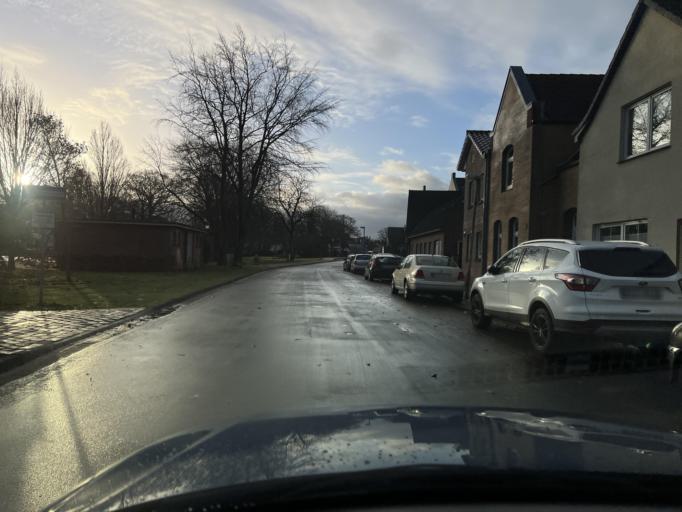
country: DE
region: Schleswig-Holstein
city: Heide
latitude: 54.1980
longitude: 9.0970
